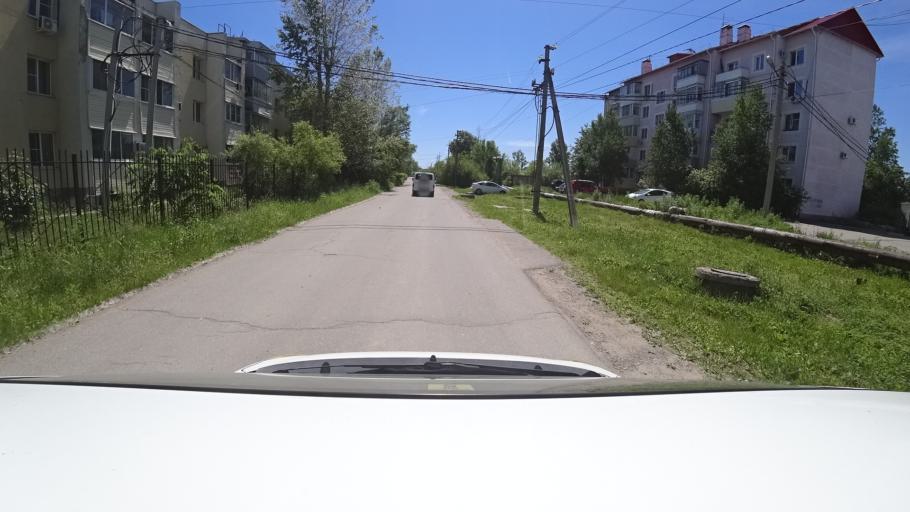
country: RU
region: Khabarovsk Krai
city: Topolevo
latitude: 48.5064
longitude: 135.1684
